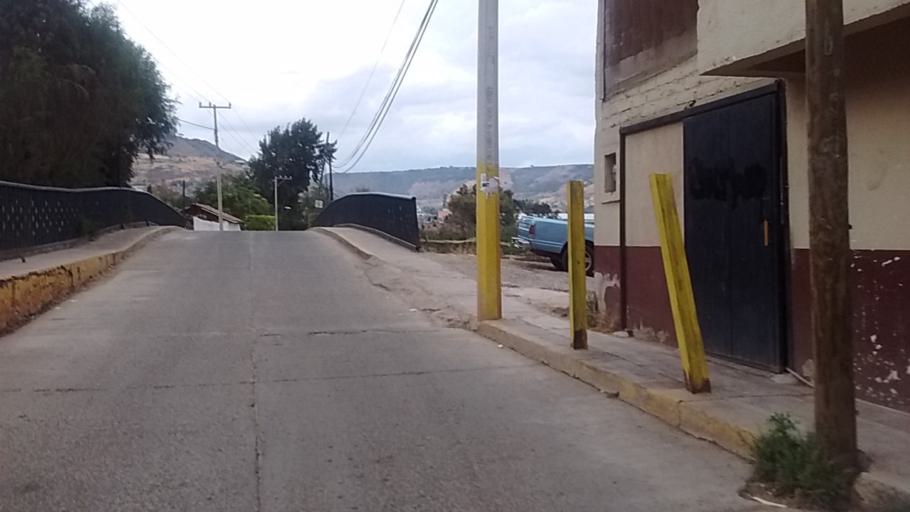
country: MX
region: Jalisco
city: Atotonilco el Alto
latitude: 20.5409
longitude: -102.5065
